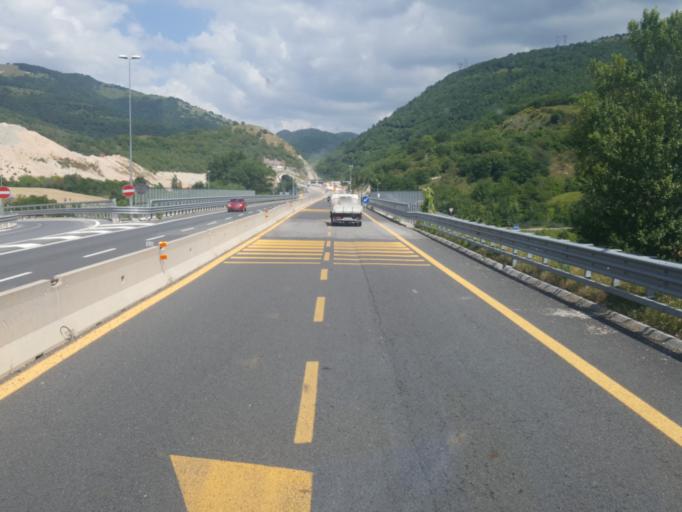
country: IT
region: Umbria
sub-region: Provincia di Perugia
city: Fossato di Vico
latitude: 43.3000
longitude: 12.7556
